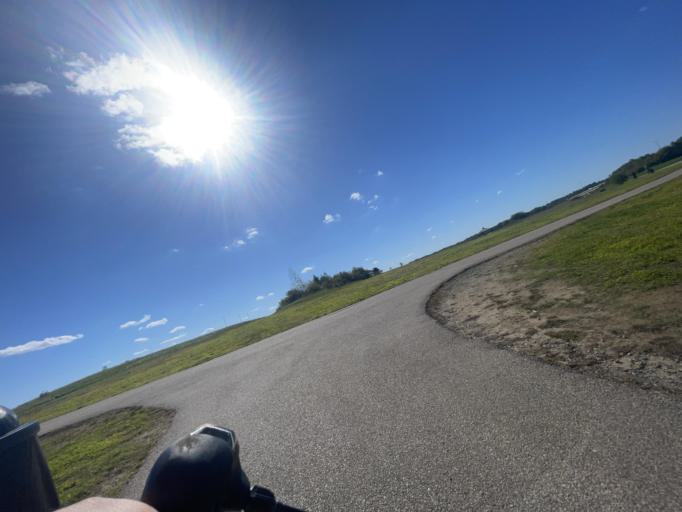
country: US
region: Massachusetts
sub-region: Norfolk County
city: Milton
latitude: 42.2804
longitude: -71.0443
